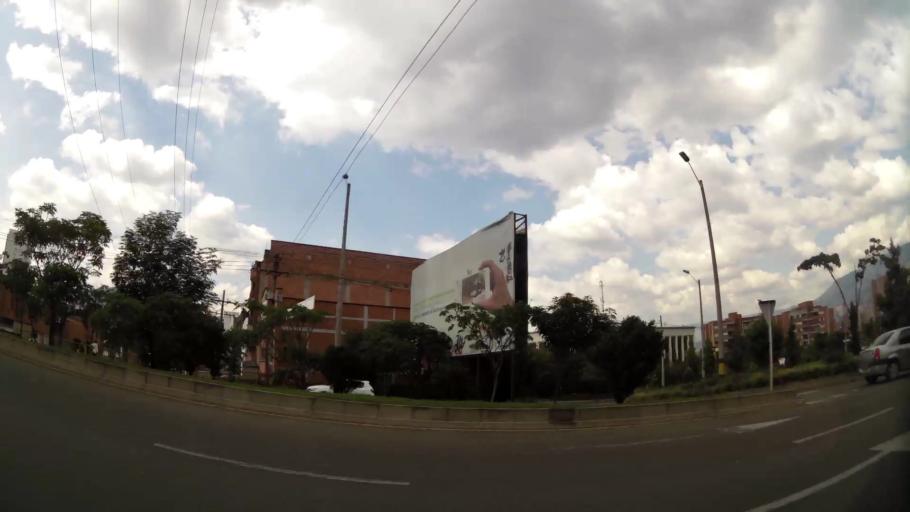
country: CO
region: Antioquia
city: Envigado
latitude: 6.1612
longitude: -75.5990
